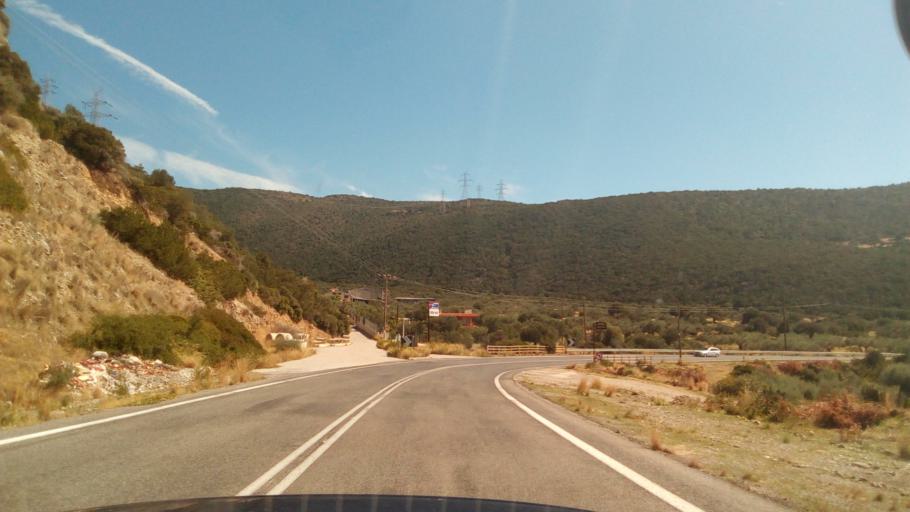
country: GR
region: West Greece
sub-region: Nomos Achaias
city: Aigio
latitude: 38.3591
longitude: 22.1383
